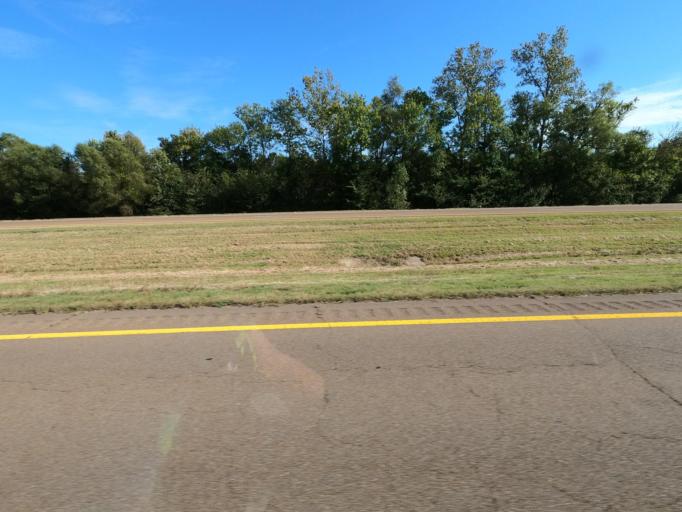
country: US
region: Tennessee
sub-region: Obion County
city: Obion
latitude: 36.1862
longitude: -89.2209
